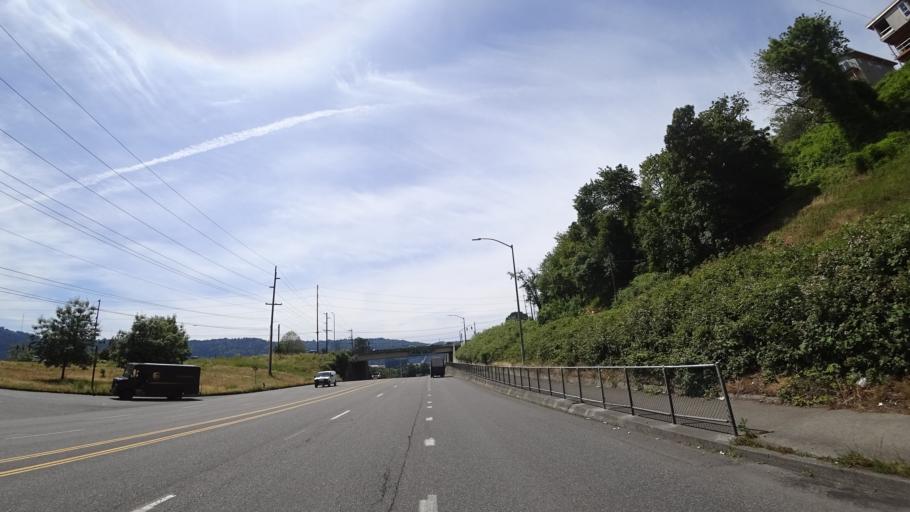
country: US
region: Oregon
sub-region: Multnomah County
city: Portland
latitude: 45.5570
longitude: -122.6909
